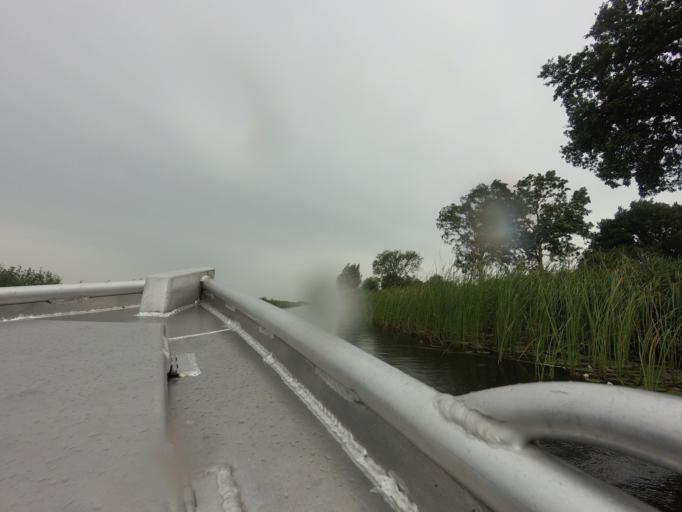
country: NL
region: Overijssel
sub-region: Gemeente Steenwijkerland
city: Blokzijl
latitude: 52.7320
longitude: 6.0134
